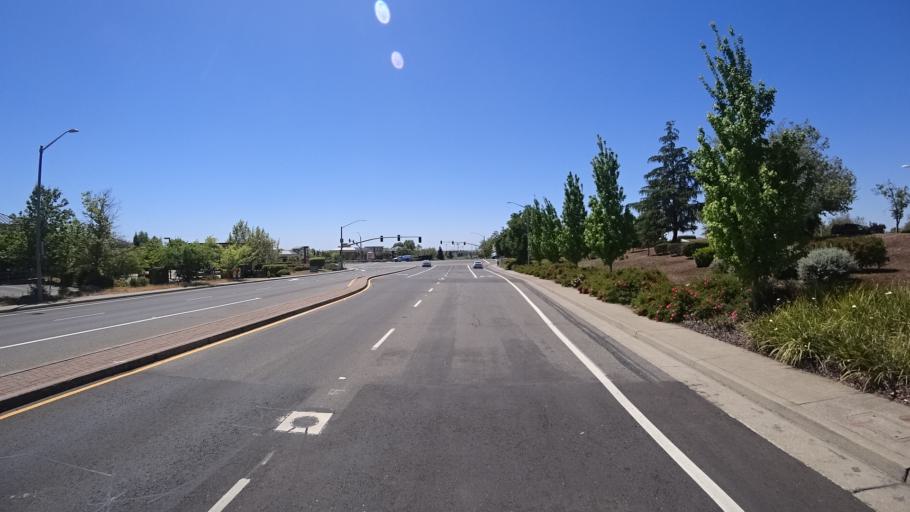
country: US
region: California
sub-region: Placer County
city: Rocklin
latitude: 38.8116
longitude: -121.2826
